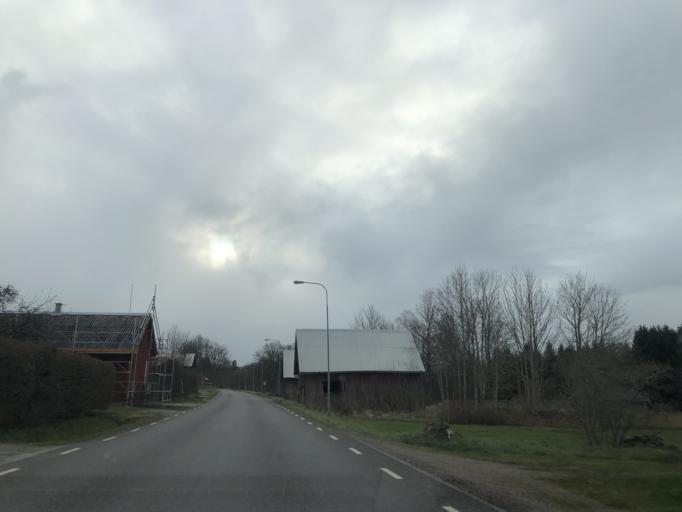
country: SE
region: Vaestra Goetaland
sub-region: Ulricehamns Kommun
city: Ulricehamn
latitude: 57.6831
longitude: 13.4145
